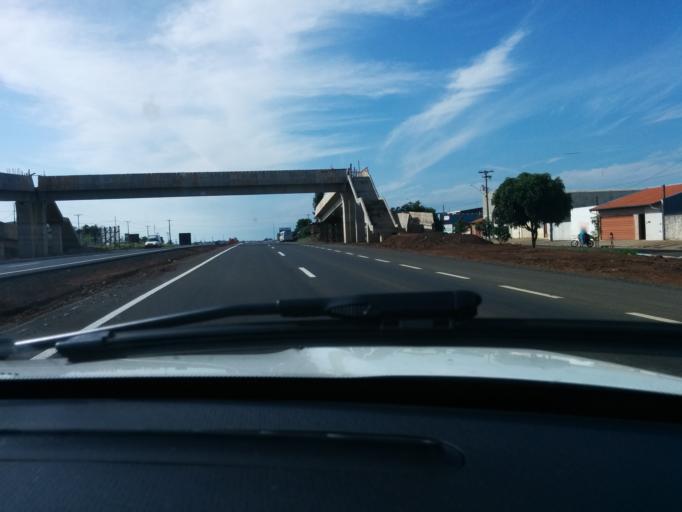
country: BR
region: Sao Paulo
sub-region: Franca
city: Franca
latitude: -20.4703
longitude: -47.4133
